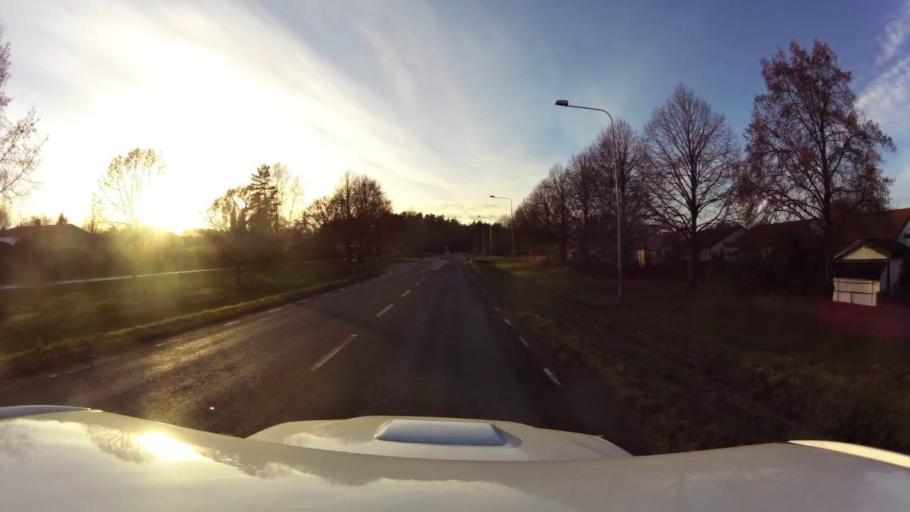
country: SE
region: OEstergoetland
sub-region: Linkopings Kommun
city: Linkoping
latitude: 58.3827
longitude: 15.6446
